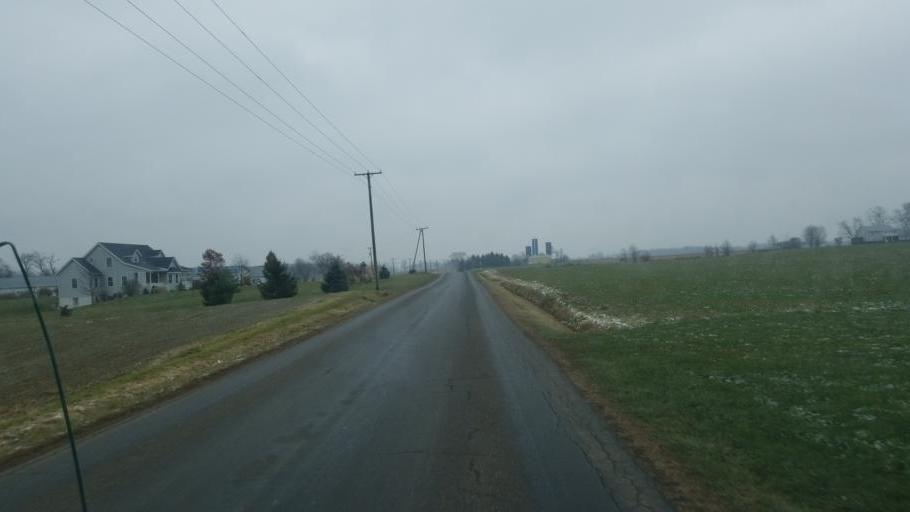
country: US
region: Ohio
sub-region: Huron County
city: Greenwich
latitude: 40.9749
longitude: -82.5748
